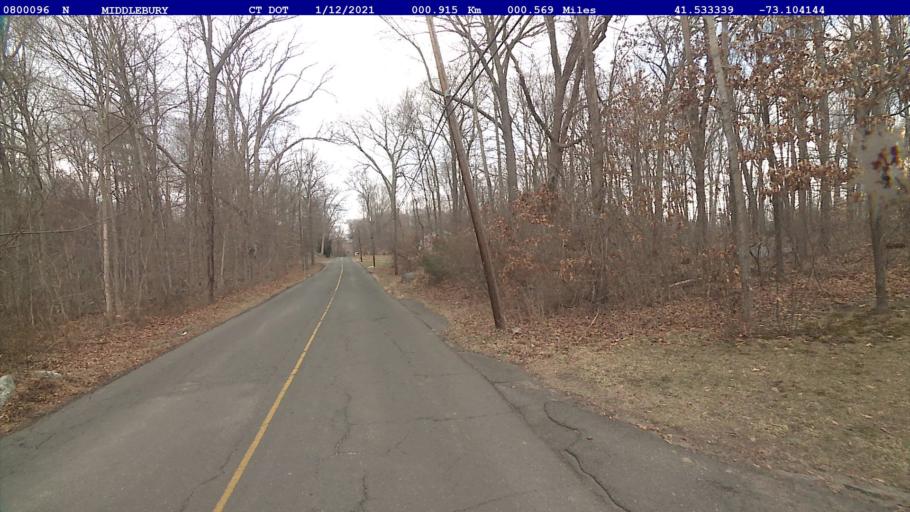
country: US
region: Connecticut
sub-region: New Haven County
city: Middlebury
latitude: 41.5333
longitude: -73.1042
